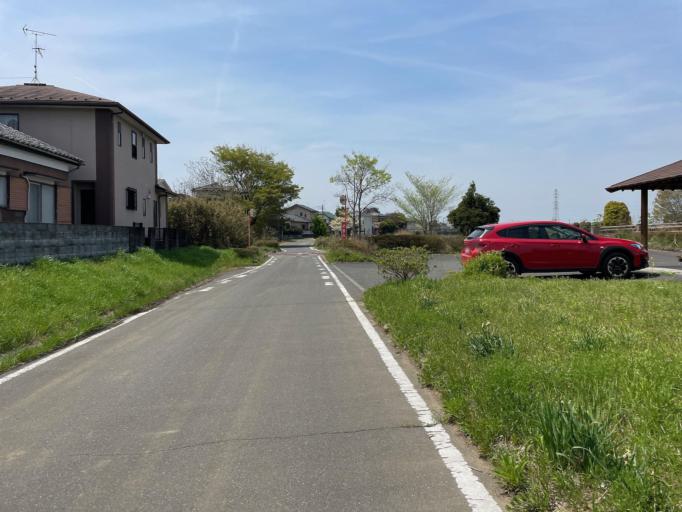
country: JP
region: Saitama
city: Fukayacho
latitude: 36.2051
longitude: 139.2977
